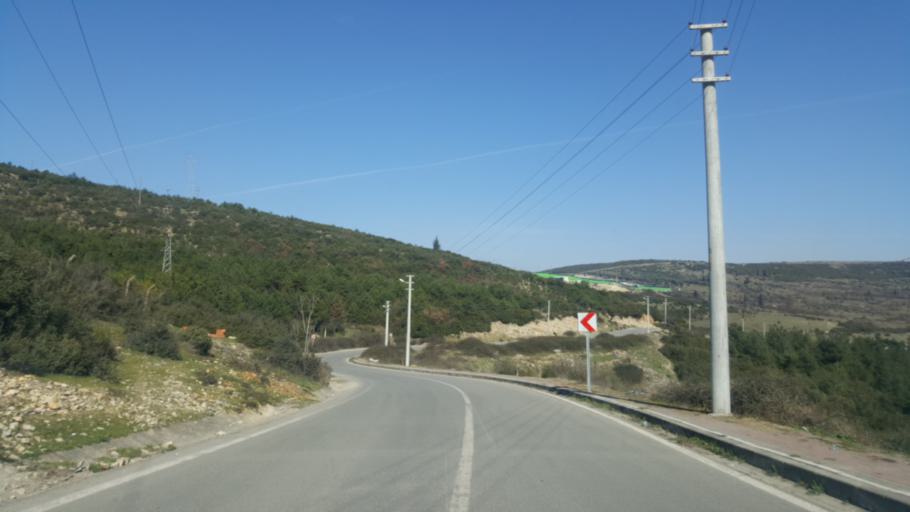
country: TR
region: Kocaeli
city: Tavsancil
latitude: 40.7870
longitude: 29.5612
